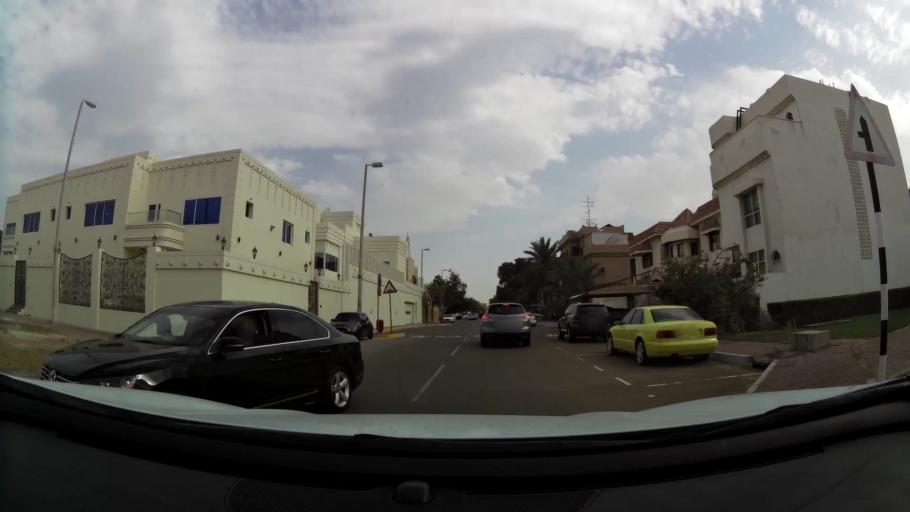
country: AE
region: Abu Dhabi
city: Abu Dhabi
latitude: 24.4635
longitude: 54.3504
